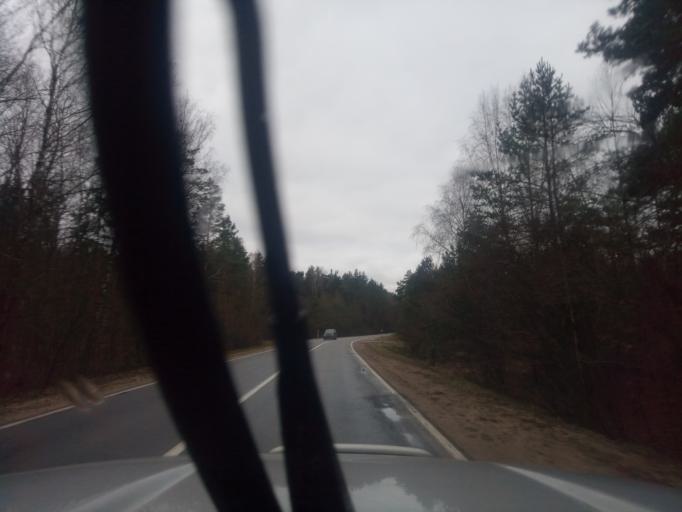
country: BY
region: Minsk
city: Kapyl'
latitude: 53.1612
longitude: 27.1149
